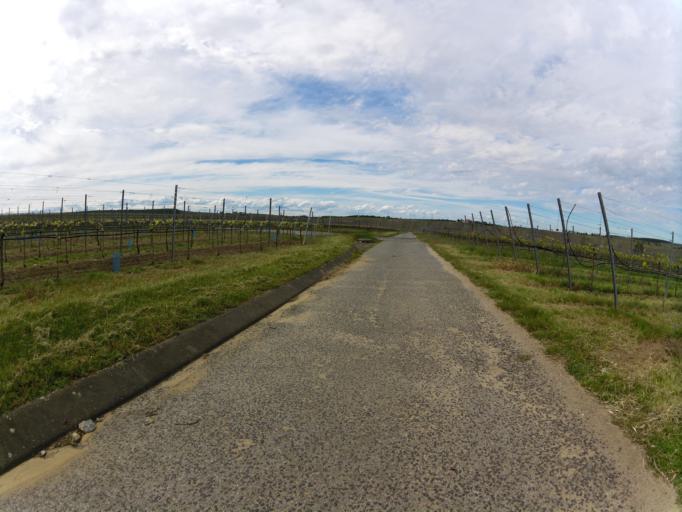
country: DE
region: Bavaria
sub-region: Regierungsbezirk Unterfranken
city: Nordheim
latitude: 49.8517
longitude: 10.1939
